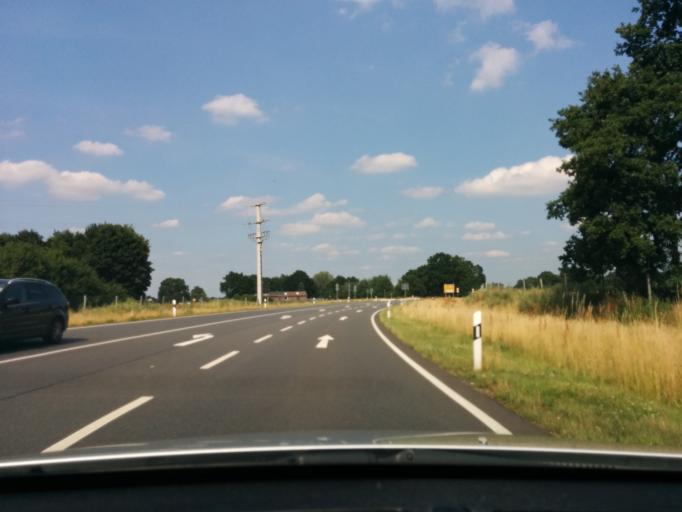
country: DE
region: North Rhine-Westphalia
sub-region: Regierungsbezirk Munster
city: Wettringen
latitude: 52.1994
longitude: 7.3008
